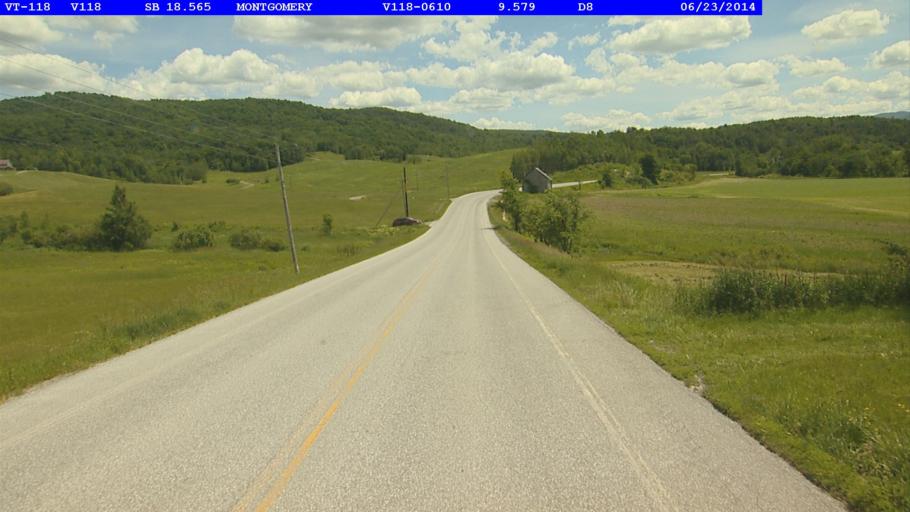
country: US
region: Vermont
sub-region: Franklin County
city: Richford
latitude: 44.9117
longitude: -72.6617
